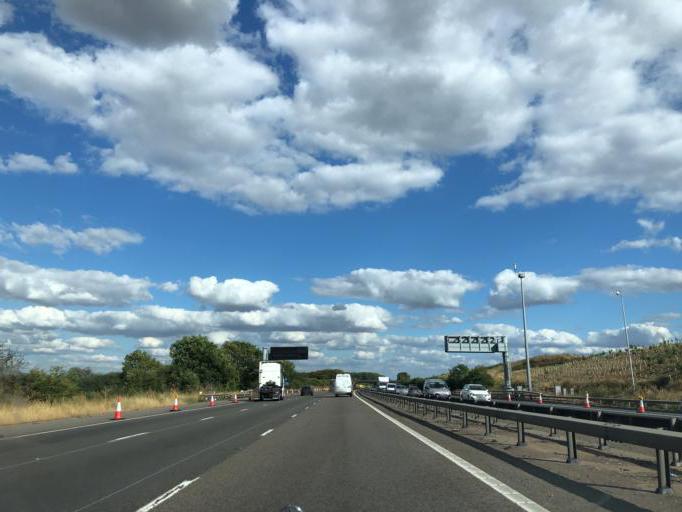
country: GB
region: England
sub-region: Milton Keynes
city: Moulsoe
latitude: 52.0493
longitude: -0.6713
